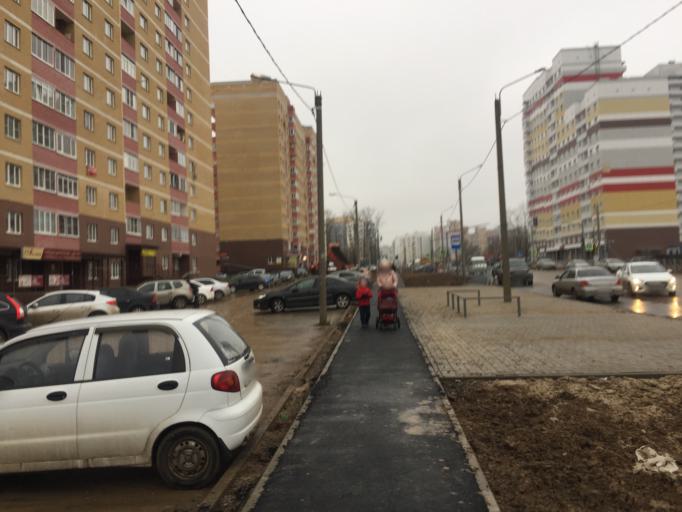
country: RU
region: Jaroslavl
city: Yaroslavl
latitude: 57.6992
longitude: 39.7892
